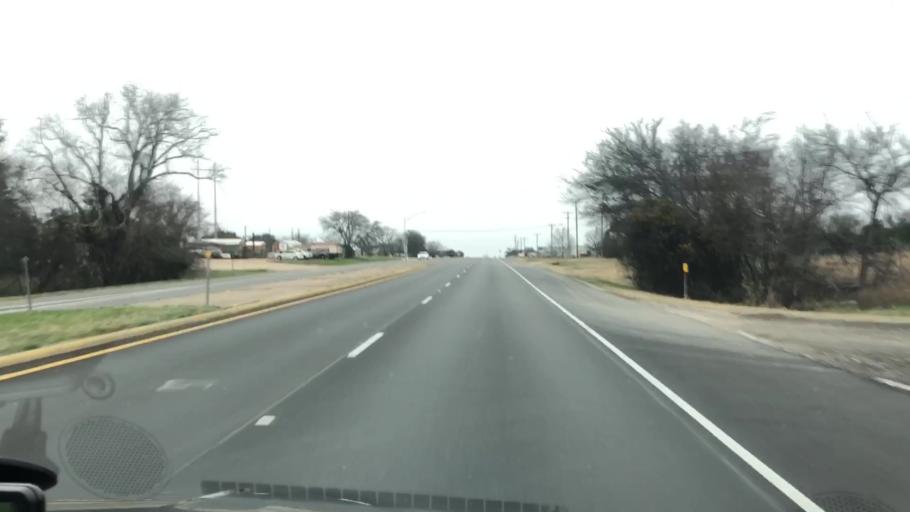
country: US
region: Texas
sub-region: Lampasas County
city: Lampasas
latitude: 31.0861
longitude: -98.1878
